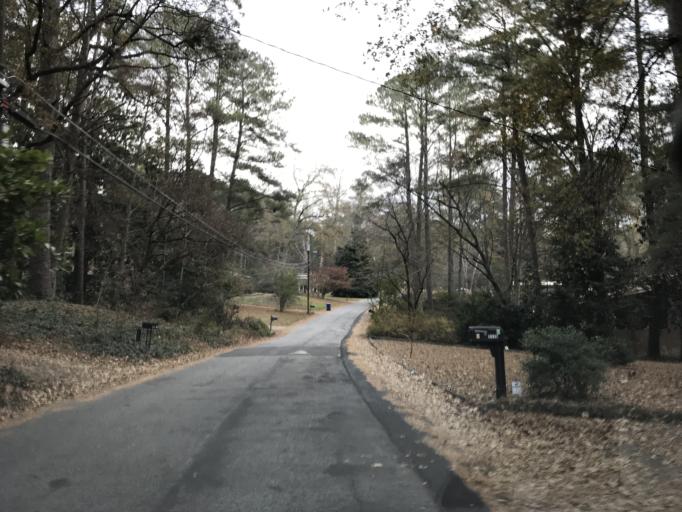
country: US
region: Georgia
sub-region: DeKalb County
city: Doraville
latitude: 33.8798
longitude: -84.2587
